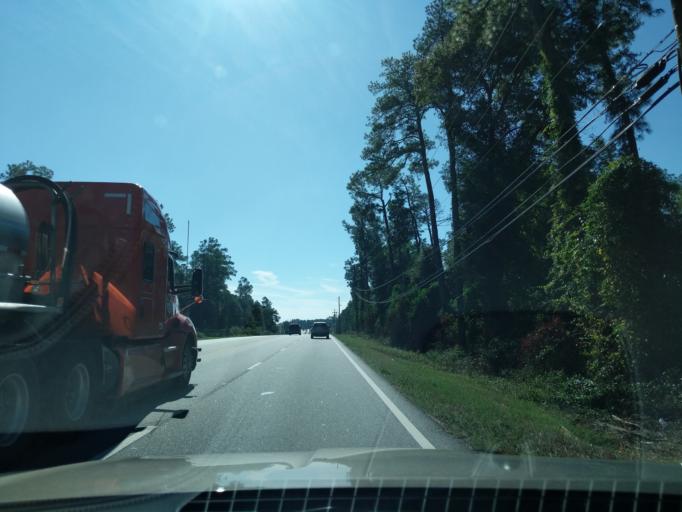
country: US
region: Georgia
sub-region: Richmond County
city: Augusta
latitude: 33.3733
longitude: -81.9991
